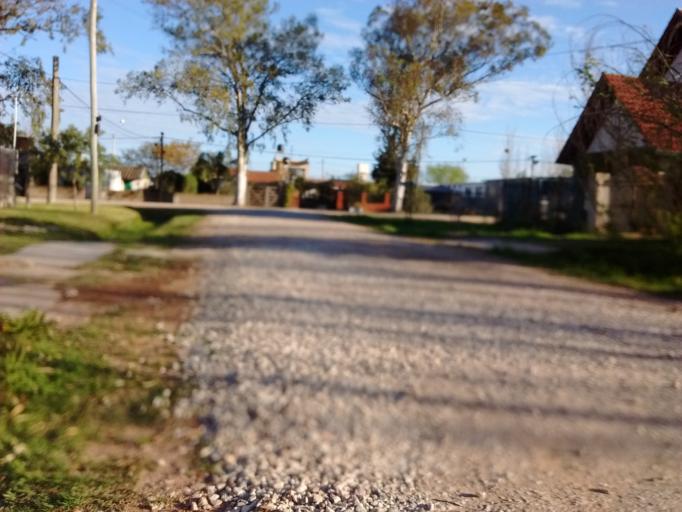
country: AR
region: Santa Fe
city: Funes
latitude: -32.9273
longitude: -60.7926
